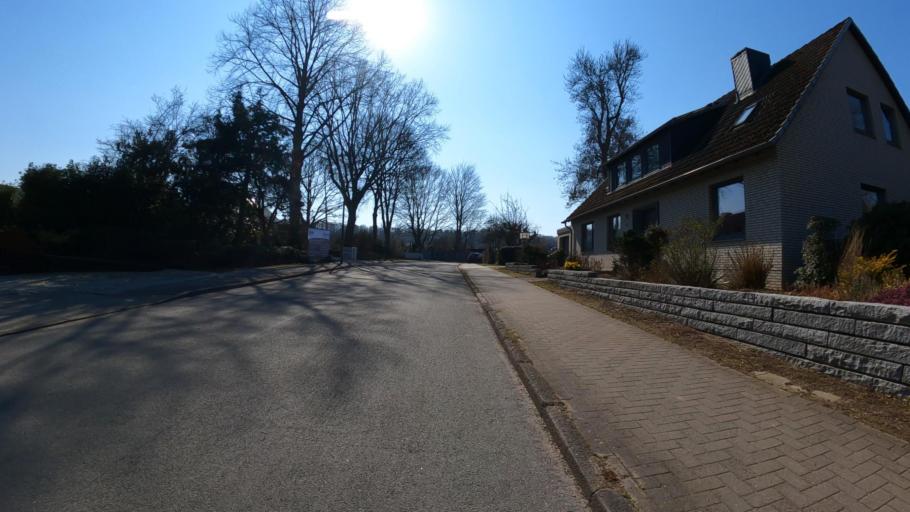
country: DE
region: Hamburg
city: Harburg
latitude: 53.4353
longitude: 9.9634
